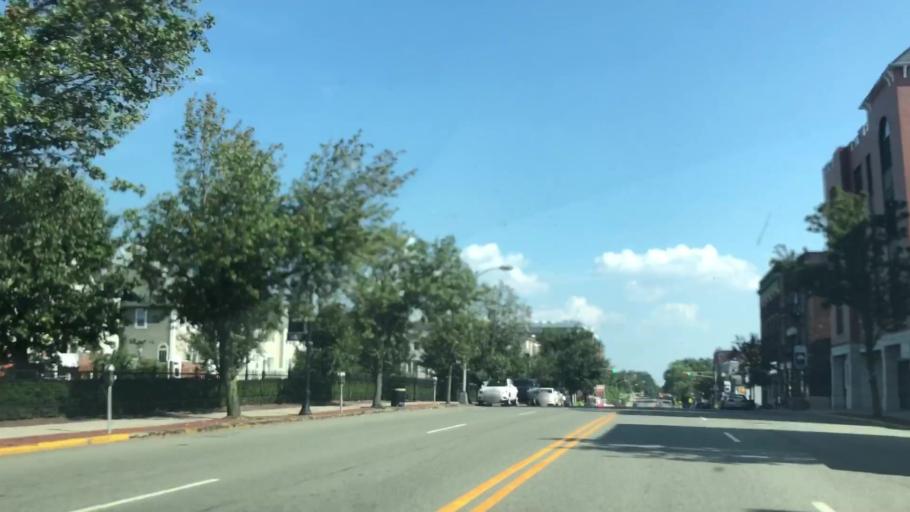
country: US
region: New Jersey
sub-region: Essex County
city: Glen Ridge
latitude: 40.8094
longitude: -74.2123
